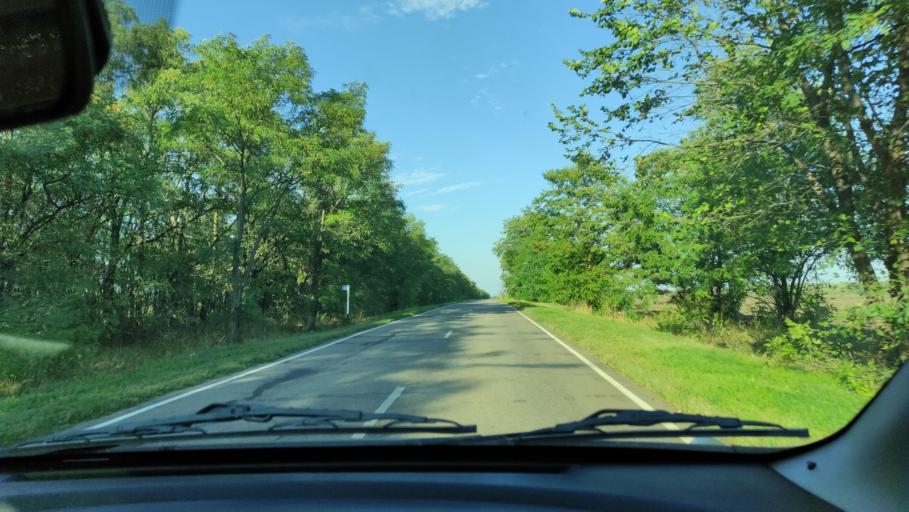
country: RU
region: Voronezj
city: Verkhniy Mamon
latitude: 50.1253
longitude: 40.3134
